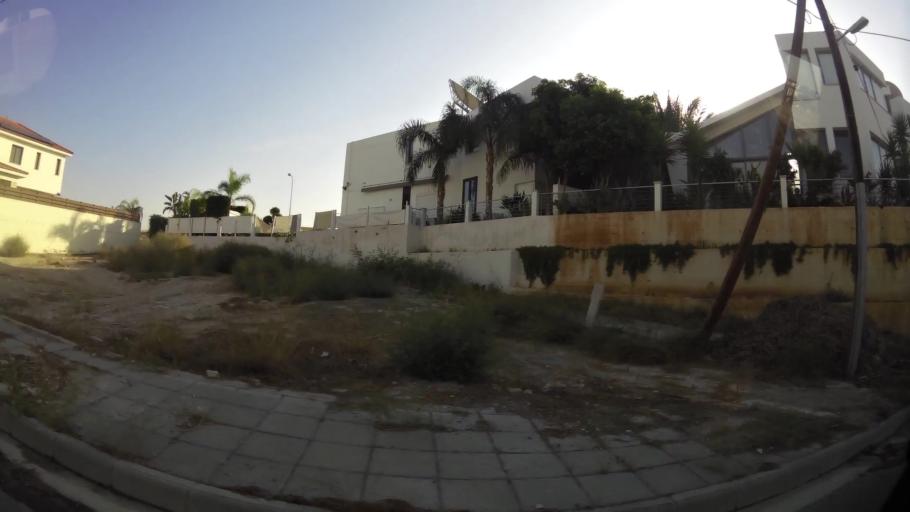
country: CY
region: Larnaka
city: Aradippou
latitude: 34.9304
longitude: 33.5941
